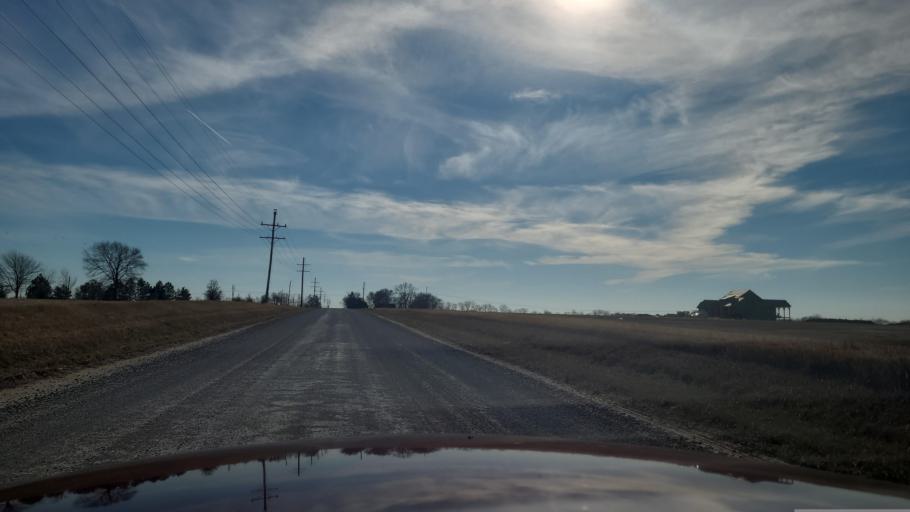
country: US
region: Kansas
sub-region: Douglas County
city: Eudora
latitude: 38.9258
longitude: -95.0748
